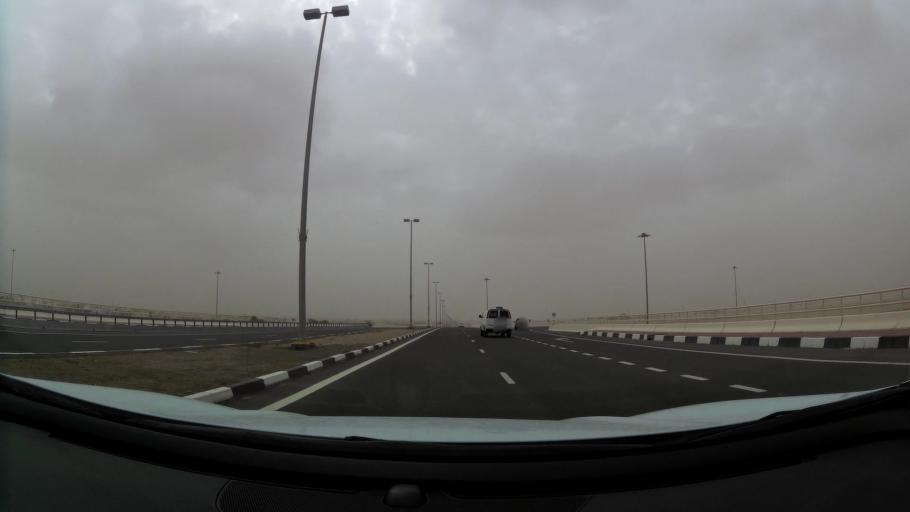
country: AE
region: Abu Dhabi
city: Abu Dhabi
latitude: 24.4133
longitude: 54.7148
